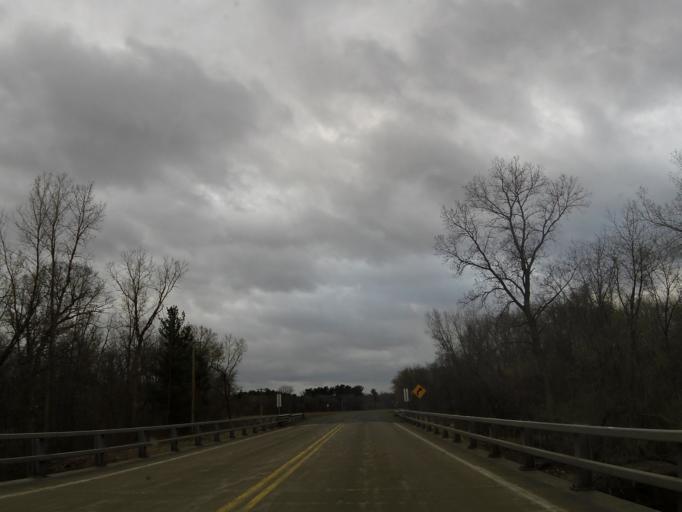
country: US
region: Wisconsin
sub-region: Saint Croix County
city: Roberts
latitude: 45.0458
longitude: -92.6223
